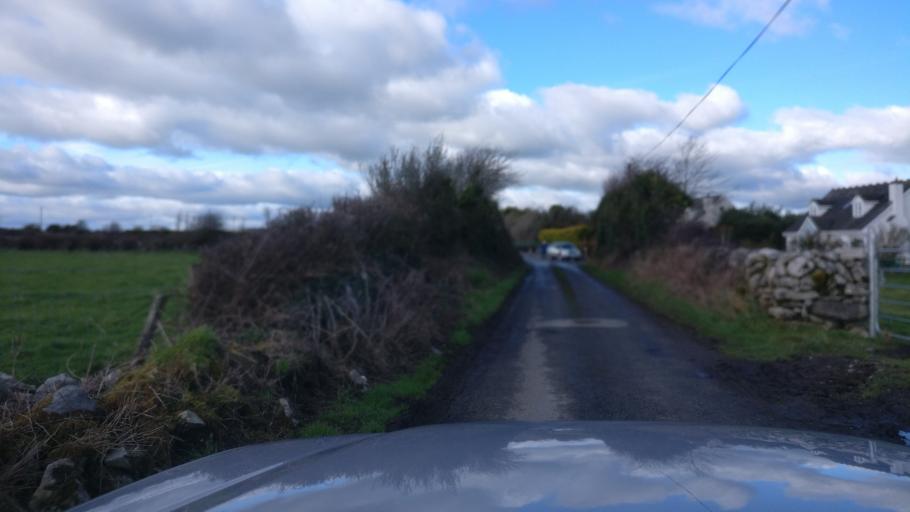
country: IE
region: Connaught
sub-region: County Galway
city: Athenry
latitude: 53.2329
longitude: -8.8015
